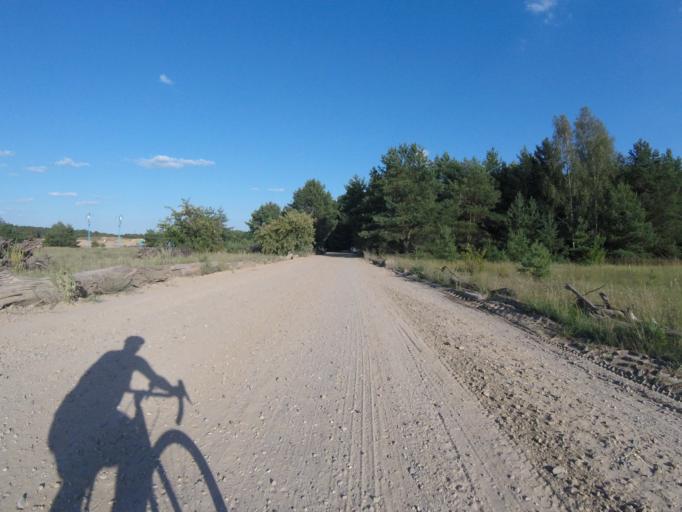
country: DE
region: Brandenburg
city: Zossen
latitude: 52.1974
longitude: 13.5080
